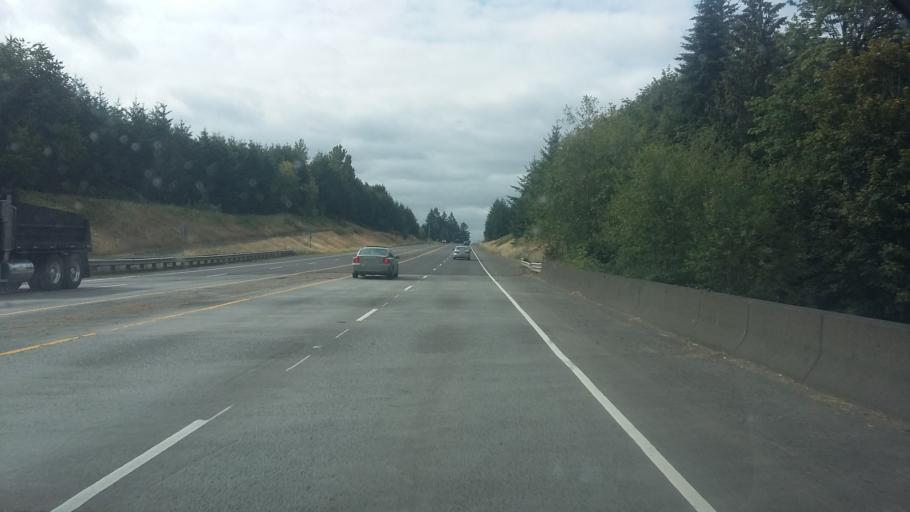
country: US
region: Washington
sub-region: Clark County
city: Brush Prairie
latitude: 45.7408
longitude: -122.5517
